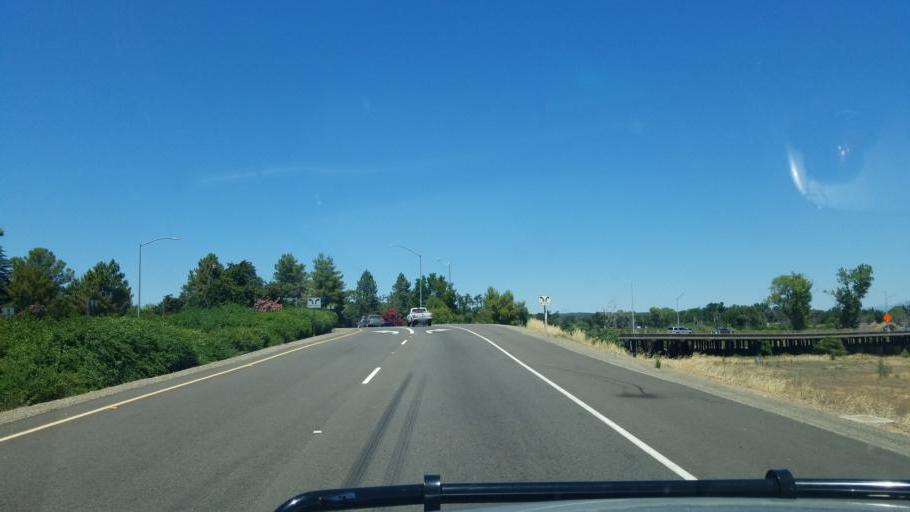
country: US
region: California
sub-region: Tehama County
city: Red Bluff
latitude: 40.1802
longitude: -122.2236
